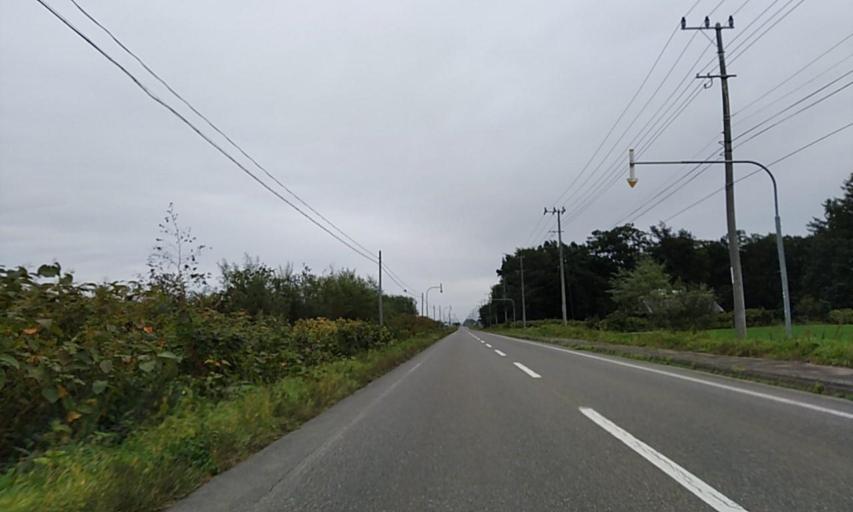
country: JP
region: Hokkaido
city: Obihiro
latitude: 42.6509
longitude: 143.1013
